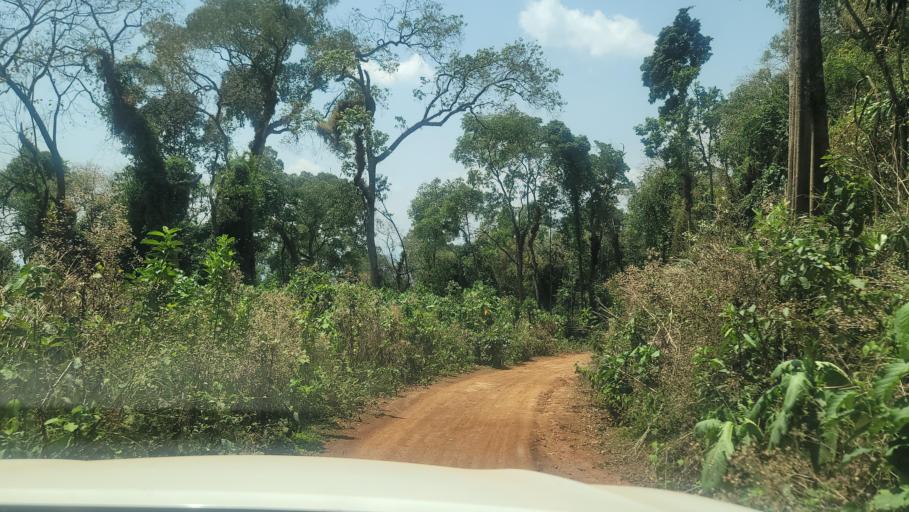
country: ET
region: Southern Nations, Nationalities, and People's Region
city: Bonga
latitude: 7.5477
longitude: 36.1753
